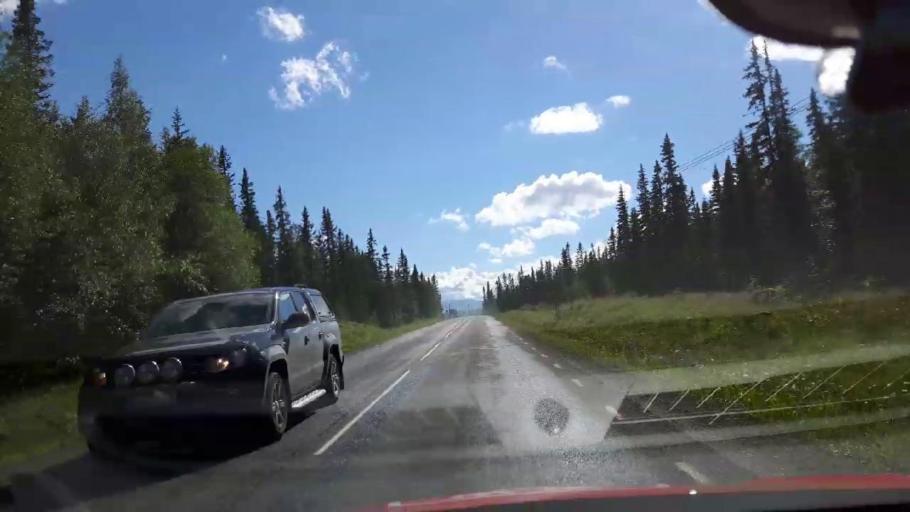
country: SE
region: Jaemtland
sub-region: Are Kommun
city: Are
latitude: 63.2312
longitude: 13.1619
